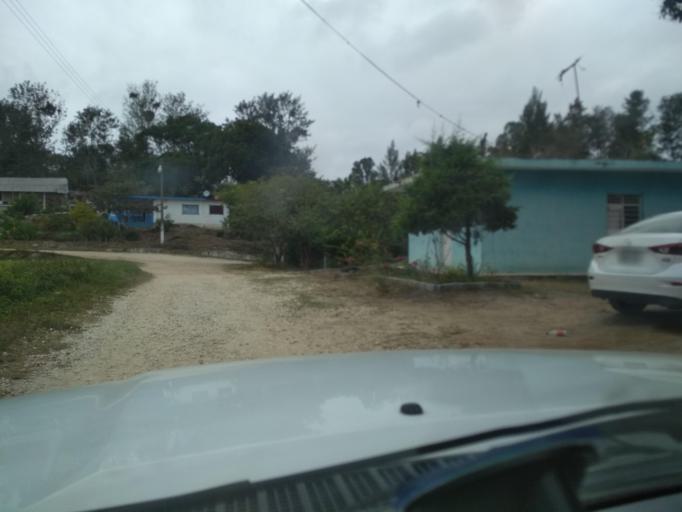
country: MX
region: Veracruz
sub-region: Emiliano Zapata
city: Dos Rios
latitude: 19.5394
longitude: -96.8007
